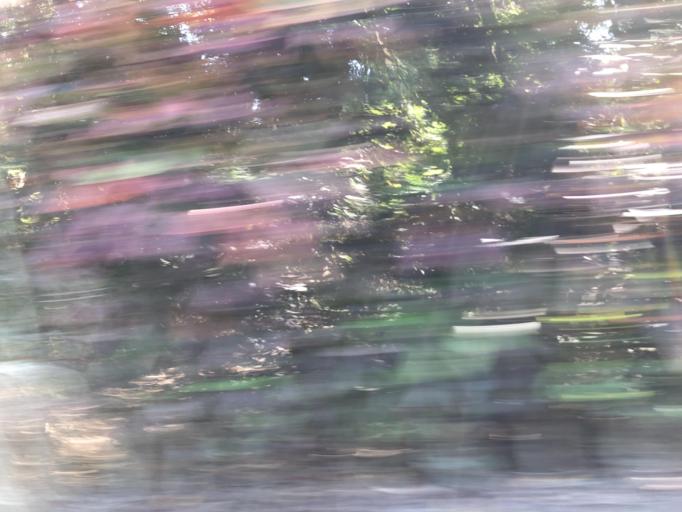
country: TW
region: Taiwan
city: Yujing
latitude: 23.0476
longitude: 120.3680
